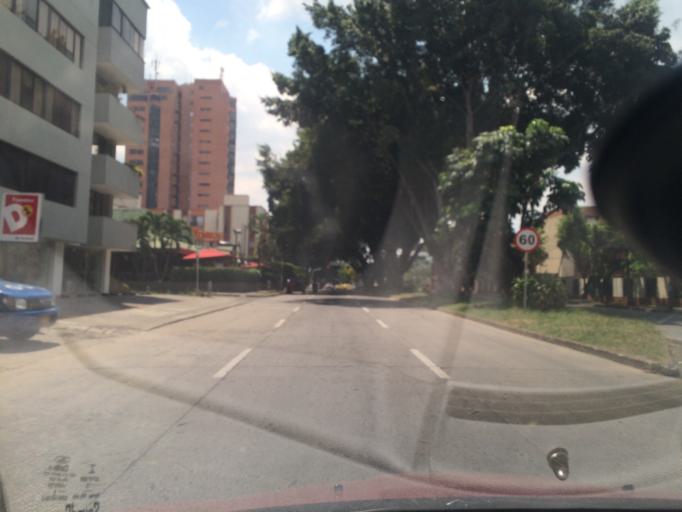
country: CO
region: Valle del Cauca
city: Cali
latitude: 3.4095
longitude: -76.5422
